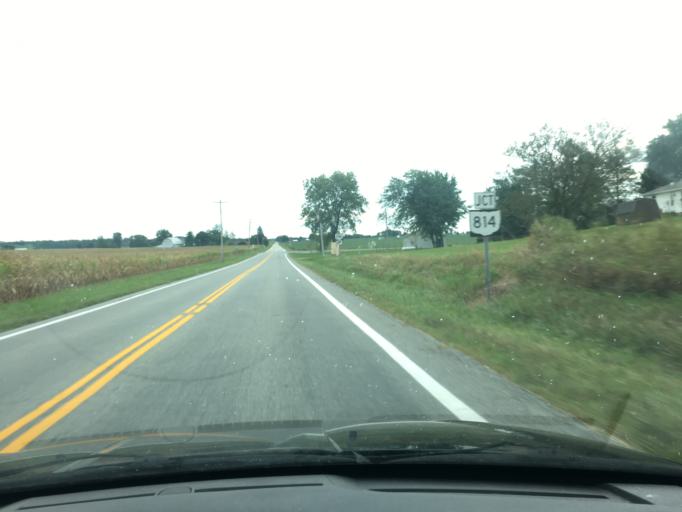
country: US
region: Ohio
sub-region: Champaign County
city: Urbana
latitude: 40.1522
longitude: -83.6825
